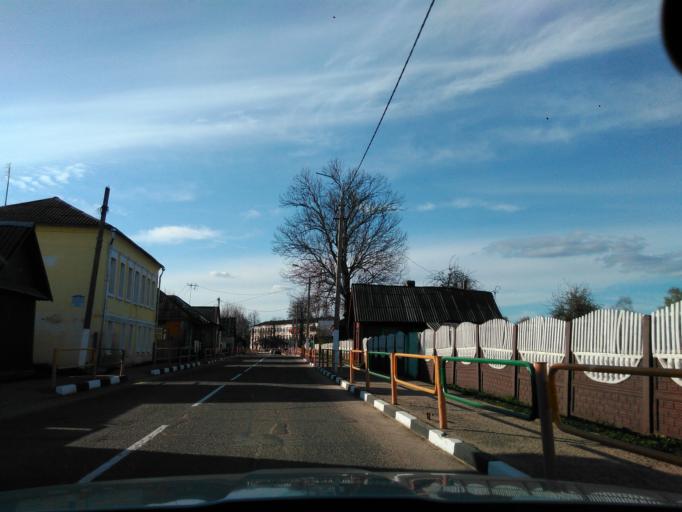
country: BY
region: Vitebsk
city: Chashniki
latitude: 54.8574
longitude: 29.1664
